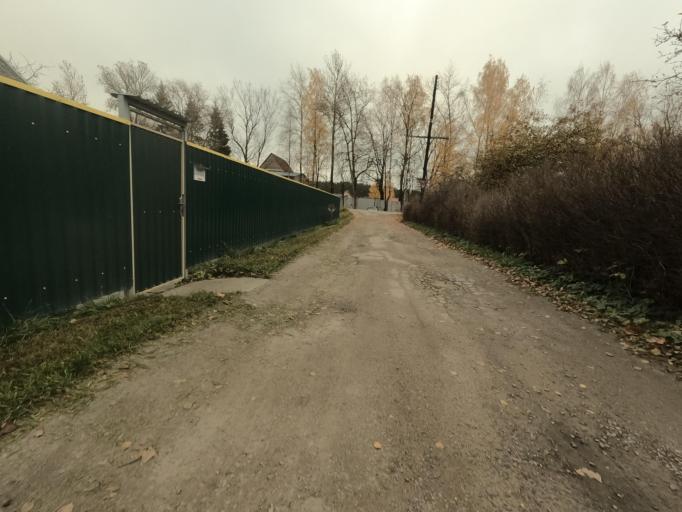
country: RU
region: Leningrad
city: Pavlovo
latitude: 59.8098
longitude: 30.8892
